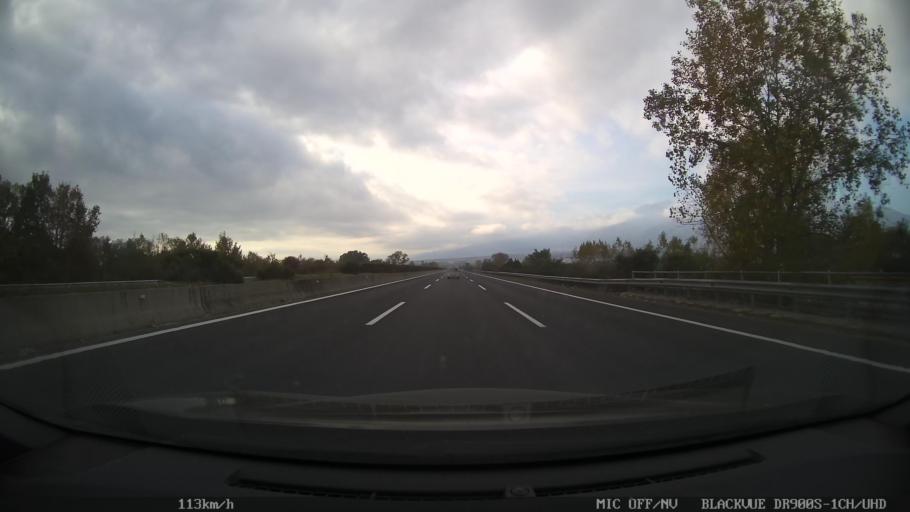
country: GR
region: Central Macedonia
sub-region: Nomos Pierias
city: Dion
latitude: 40.1644
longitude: 22.5460
